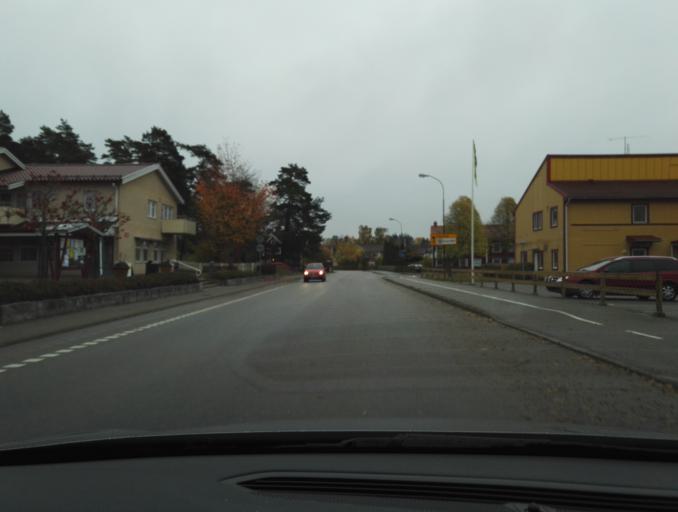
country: SE
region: Kronoberg
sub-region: Vaxjo Kommun
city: Rottne
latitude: 57.0221
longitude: 14.8925
